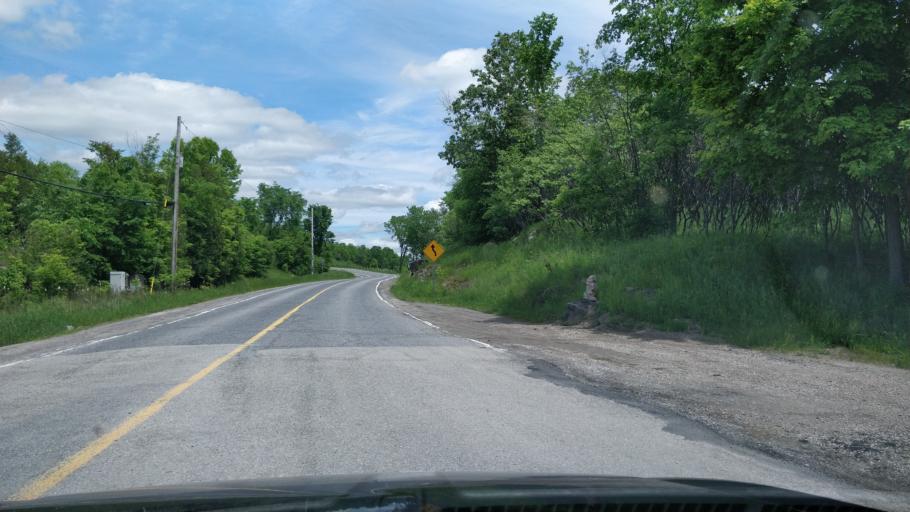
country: CA
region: Ontario
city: Perth
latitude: 44.7393
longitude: -76.5002
